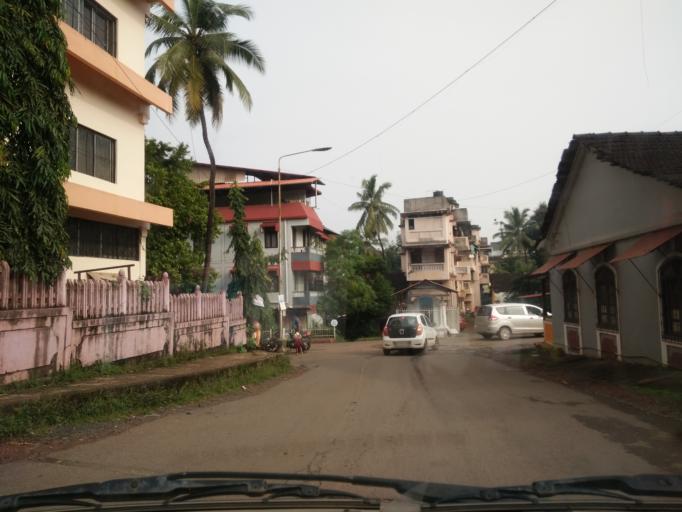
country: IN
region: Goa
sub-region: South Goa
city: Madgaon
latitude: 15.2765
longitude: 73.9556
